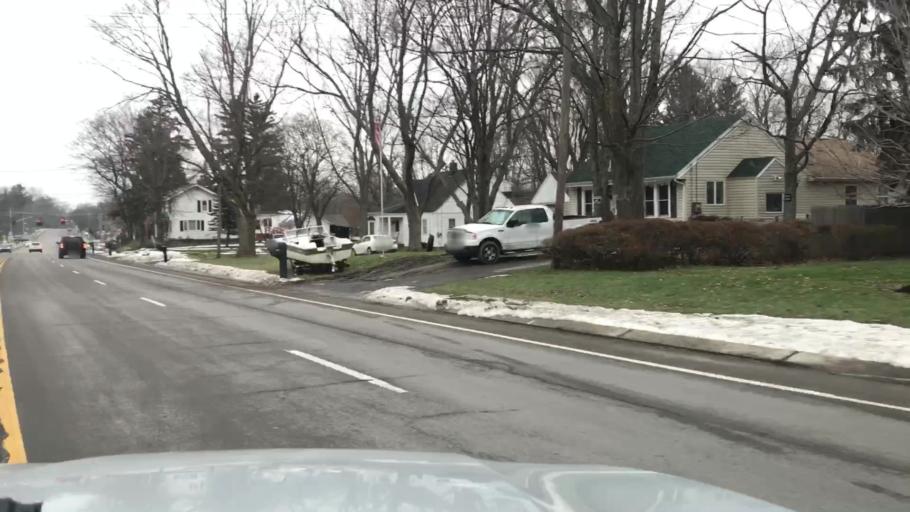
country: US
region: New York
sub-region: Erie County
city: Orchard Park
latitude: 42.7473
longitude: -78.7483
